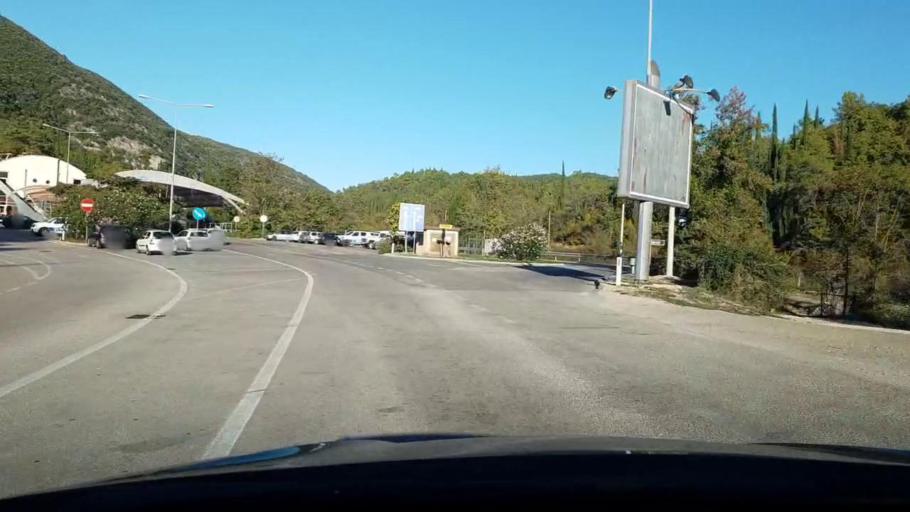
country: ME
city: Igalo
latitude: 42.4810
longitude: 18.4573
